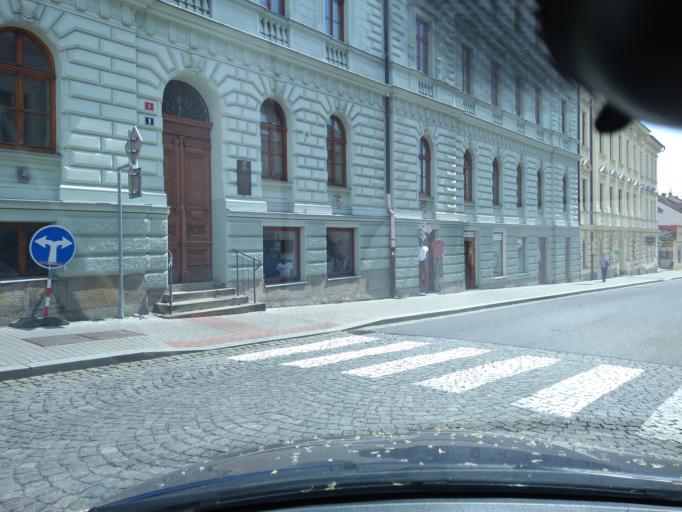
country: CZ
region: Plzensky
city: Klatovy
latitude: 49.3936
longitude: 13.2943
